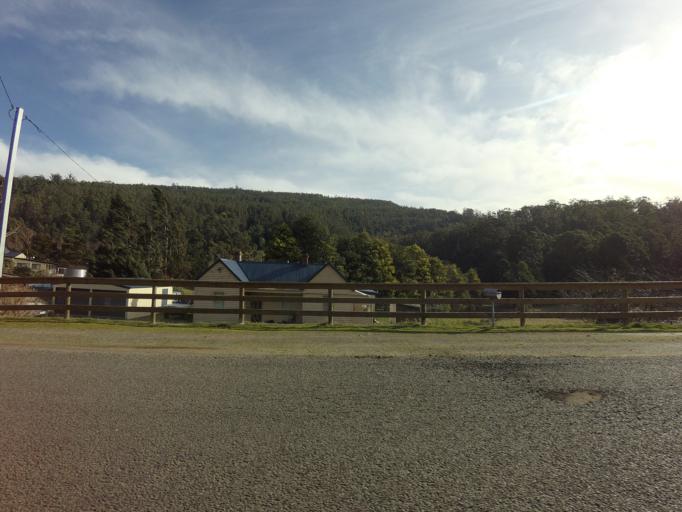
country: AU
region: Tasmania
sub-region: Huon Valley
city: Huonville
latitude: -43.0464
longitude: 147.1151
